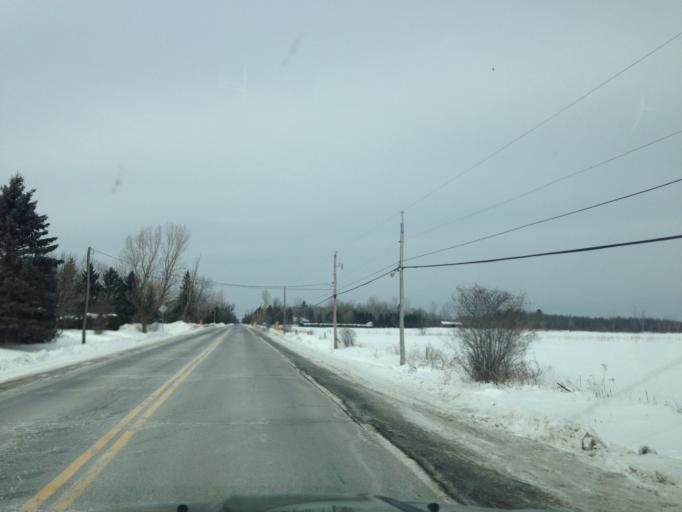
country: CA
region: Ontario
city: Ottawa
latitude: 45.3179
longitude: -75.5377
